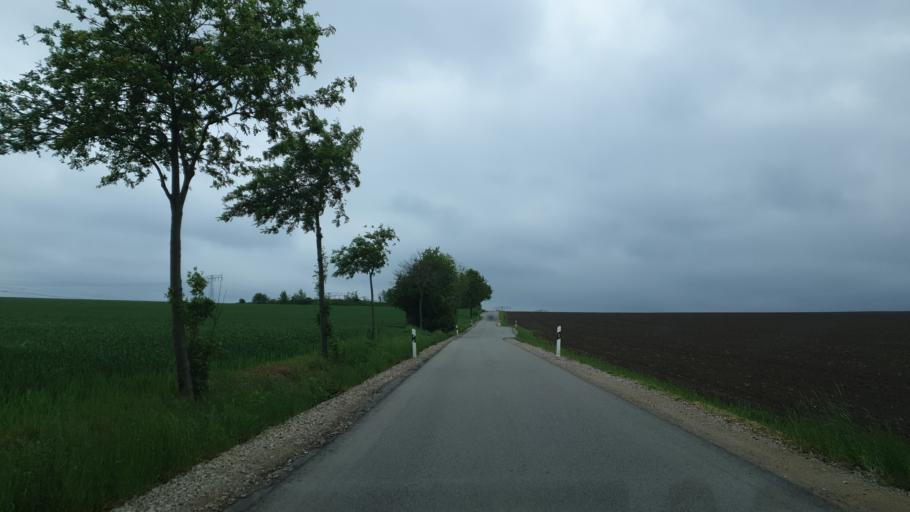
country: DE
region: Saxony
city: Limbach-Oberfrohna
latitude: 50.8557
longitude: 12.8055
